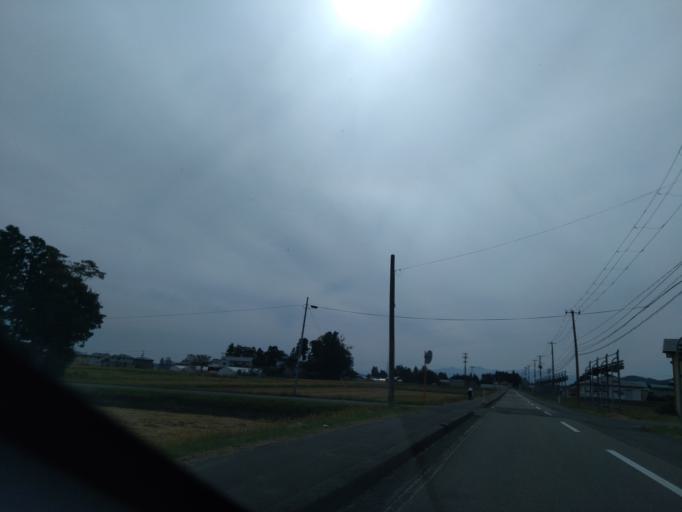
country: JP
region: Iwate
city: Hanamaki
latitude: 39.4428
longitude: 141.0842
